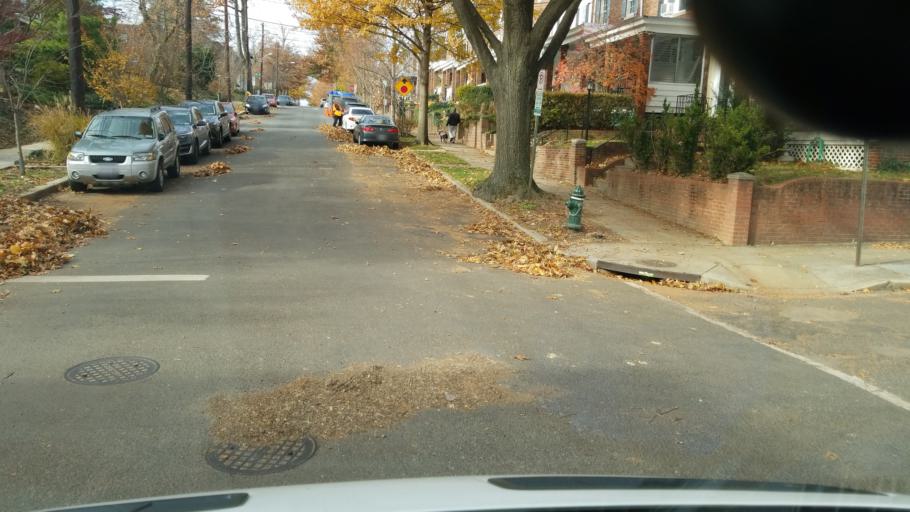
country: US
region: Maryland
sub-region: Montgomery County
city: Friendship Village
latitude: 38.9192
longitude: -77.0760
